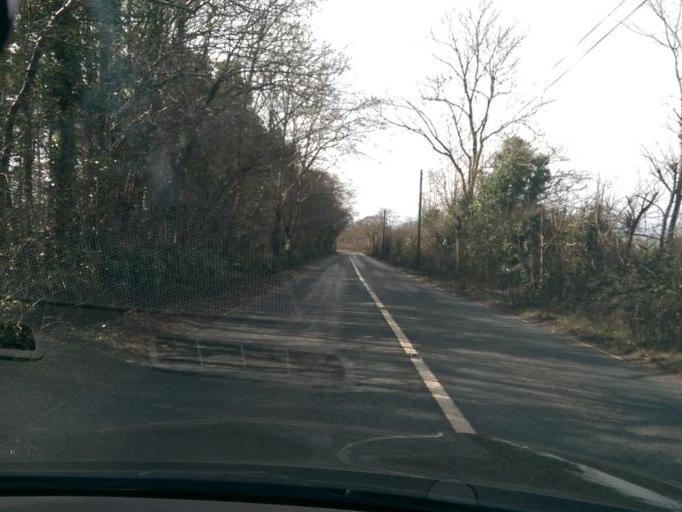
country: IE
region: Connaught
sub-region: County Galway
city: Tuam
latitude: 53.4441
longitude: -8.7205
